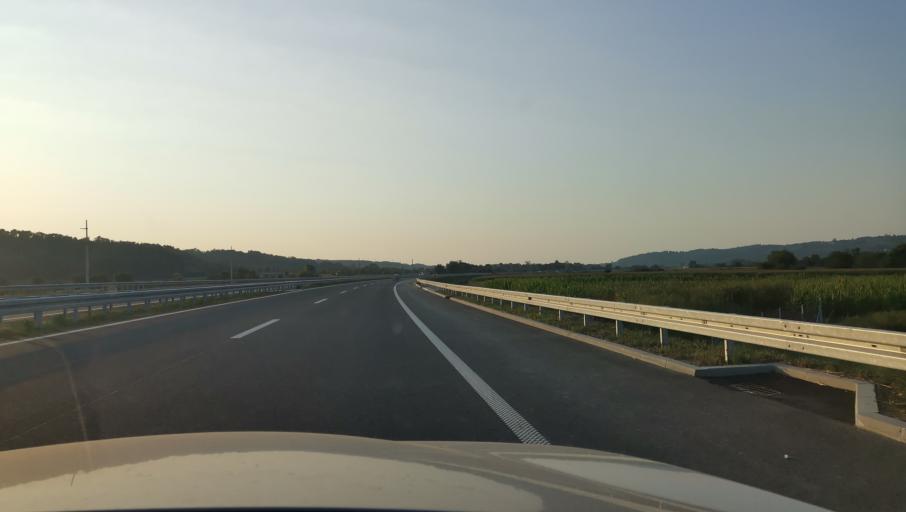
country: RS
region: Central Serbia
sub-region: Kolubarski Okrug
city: Lajkovac
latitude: 44.3118
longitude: 20.2193
